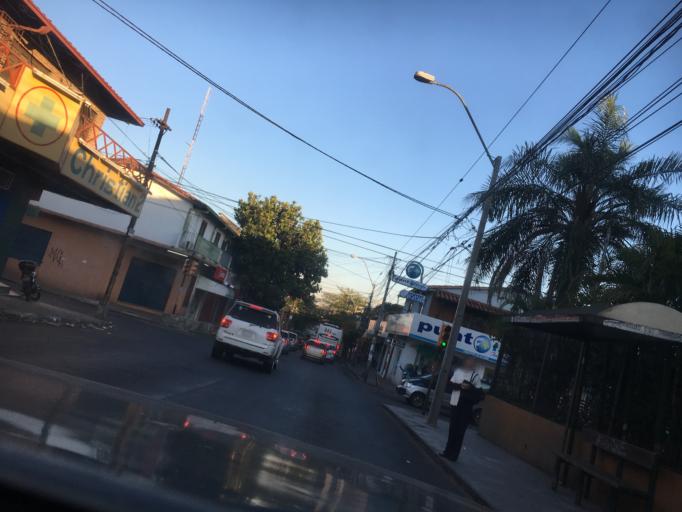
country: PY
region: Asuncion
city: Asuncion
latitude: -25.2944
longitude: -57.6422
